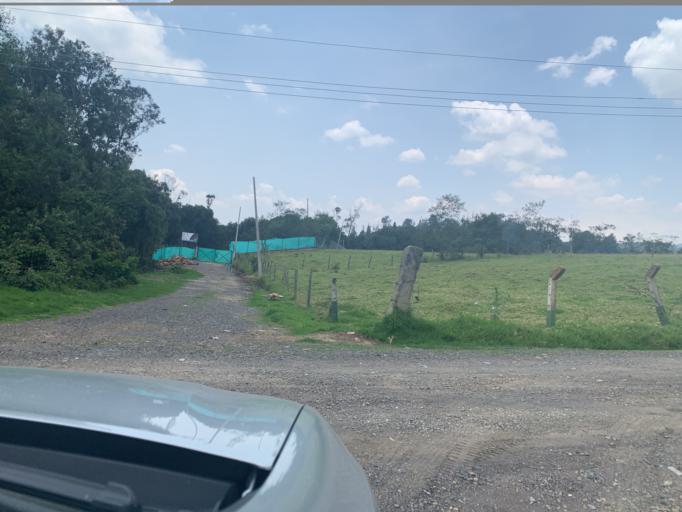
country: CO
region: Boyaca
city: Raquira
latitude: 5.5167
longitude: -73.7226
